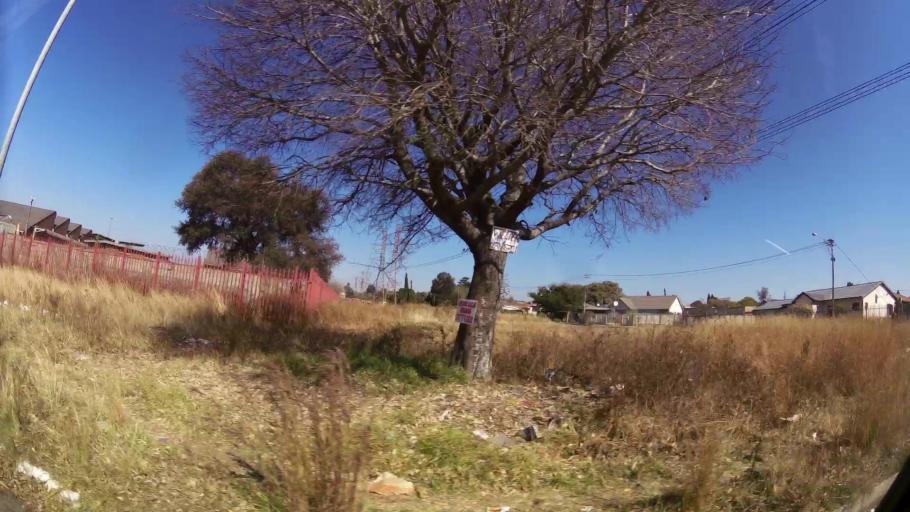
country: ZA
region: Gauteng
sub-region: City of Johannesburg Metropolitan Municipality
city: Johannesburg
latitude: -26.2488
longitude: 28.1000
